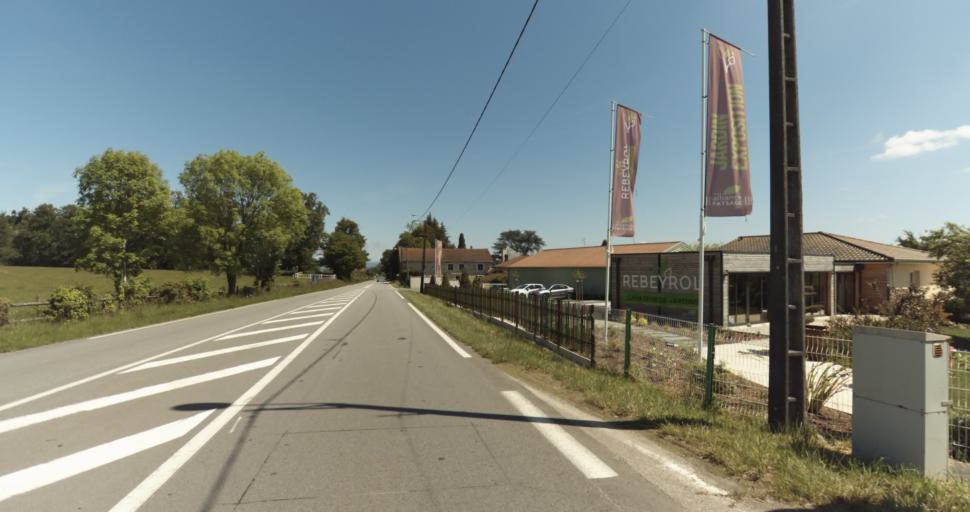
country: FR
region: Limousin
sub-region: Departement de la Haute-Vienne
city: Condat-sur-Vienne
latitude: 45.7867
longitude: 1.2897
